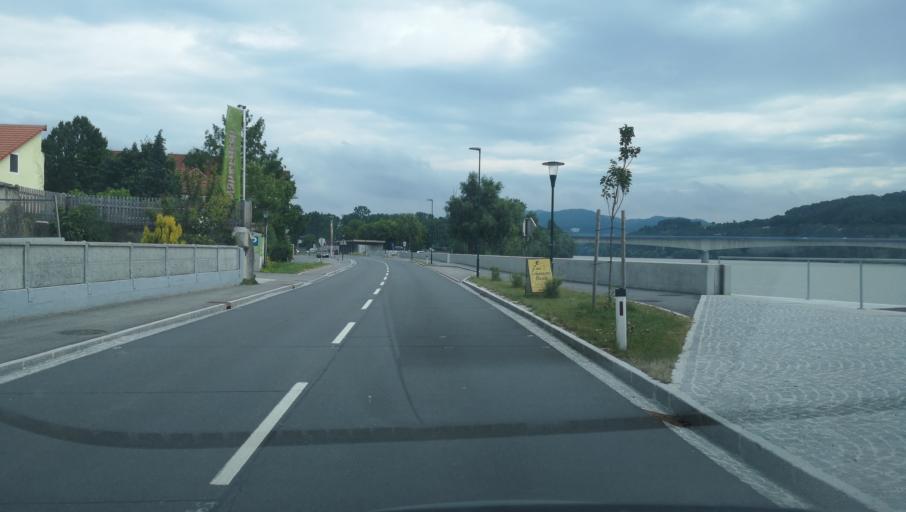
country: AT
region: Lower Austria
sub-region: Politischer Bezirk Melk
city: Emmersdorf an der Donau
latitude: 48.2409
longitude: 15.3372
